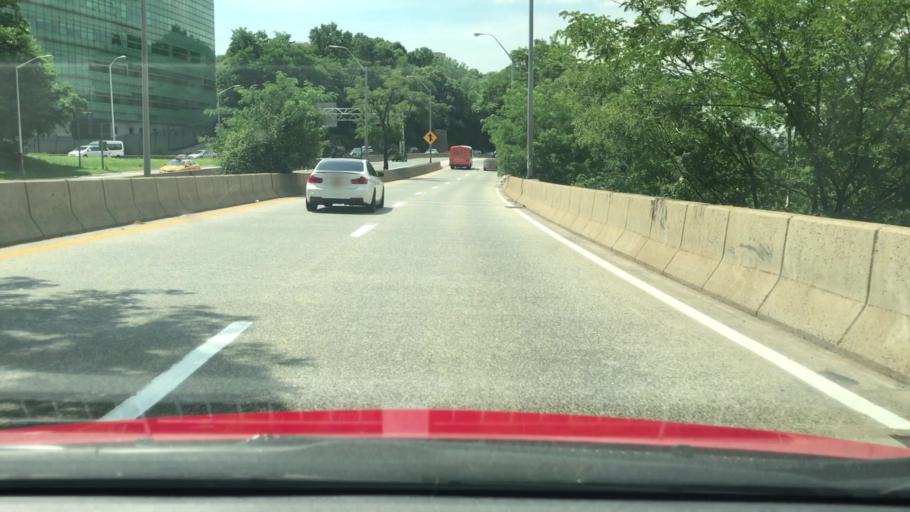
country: US
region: New Jersey
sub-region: Bergen County
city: Fort Lee
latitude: 40.8448
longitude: -73.9467
